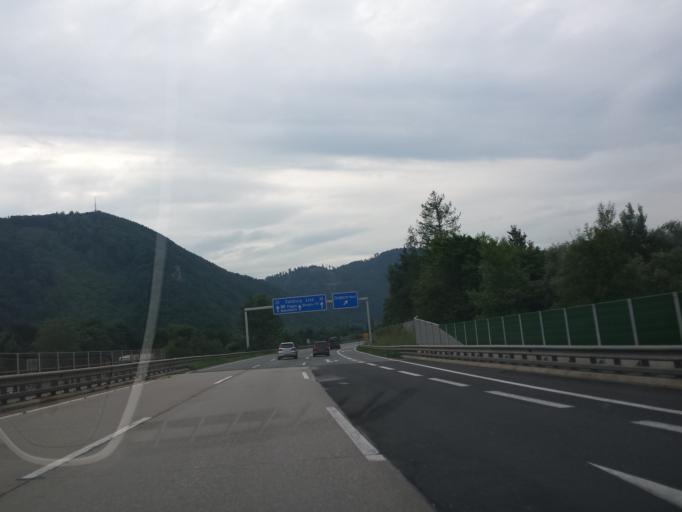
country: AT
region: Styria
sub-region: Politischer Bezirk Graz-Umgebung
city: Gratkorn
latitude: 47.1447
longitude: 15.3328
